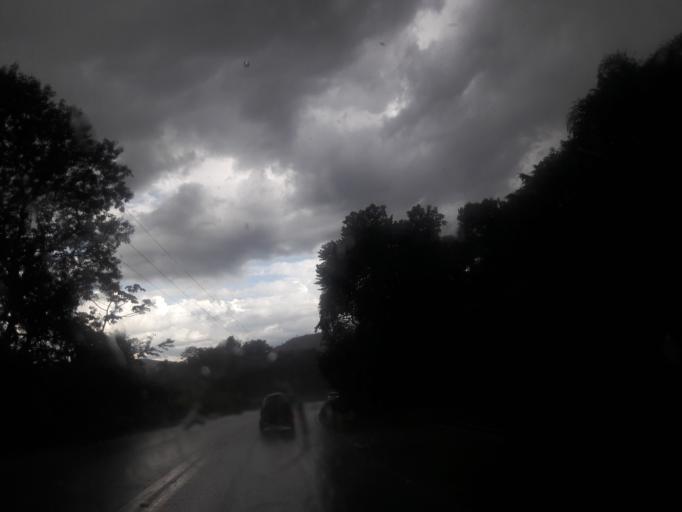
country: BR
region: Sao Paulo
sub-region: Bom Jesus Dos Perdoes
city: Bom Jesus dos Perdoes
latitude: -23.2051
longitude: -46.3900
